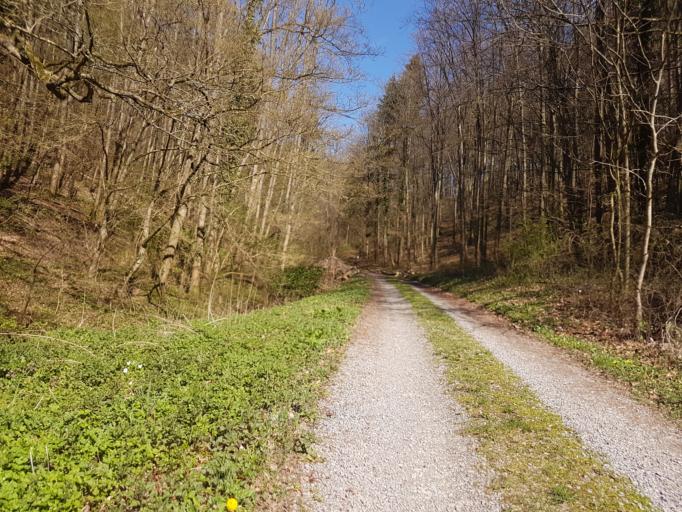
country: DE
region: Baden-Wuerttemberg
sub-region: Regierungsbezirk Stuttgart
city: Jagsthausen
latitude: 49.3323
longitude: 9.4891
